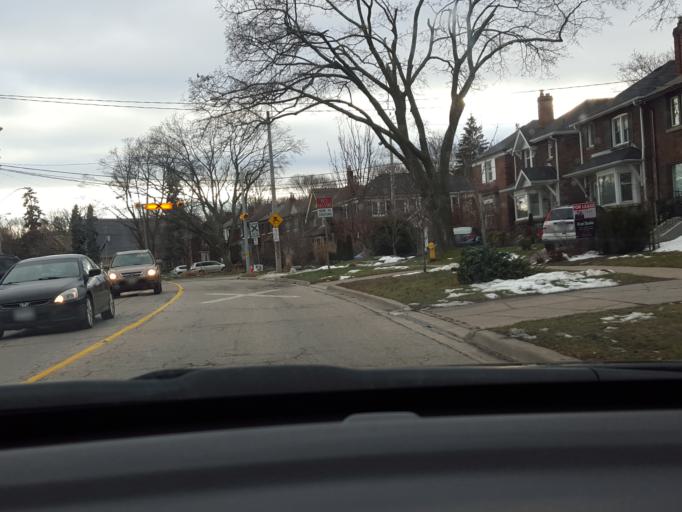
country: CA
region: Ontario
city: Toronto
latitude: 43.7071
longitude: -79.3675
